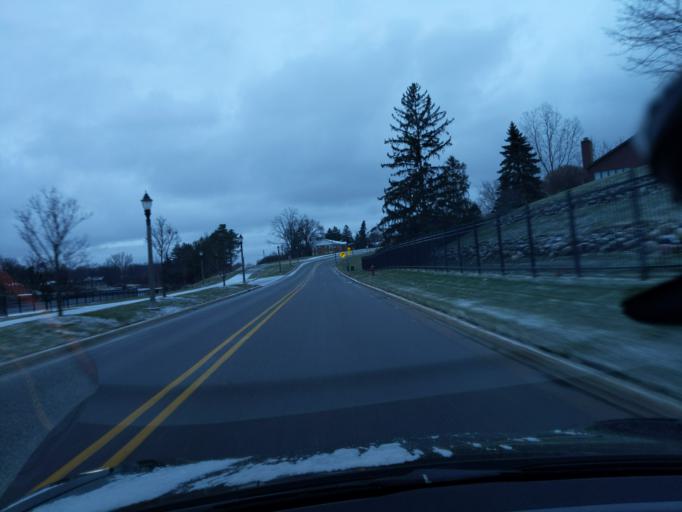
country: US
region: Michigan
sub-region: Eaton County
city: Waverly
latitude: 42.7107
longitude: -84.5995
